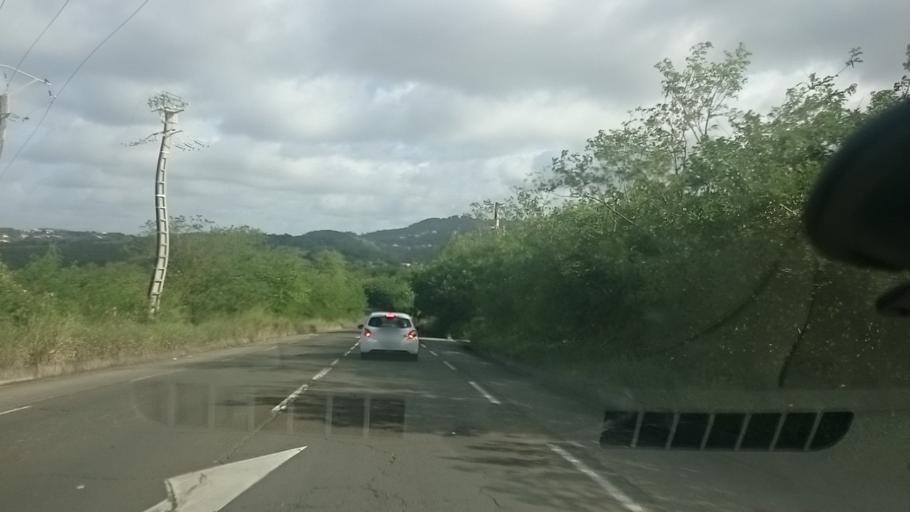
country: MQ
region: Martinique
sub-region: Martinique
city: Le Vauclin
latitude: 14.5776
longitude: -60.8640
